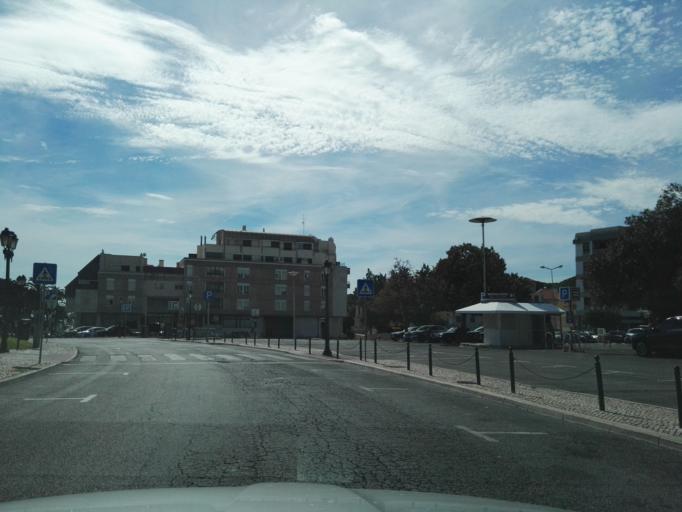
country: PT
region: Lisbon
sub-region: Cascais
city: Estoril
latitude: 38.7077
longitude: -9.3983
